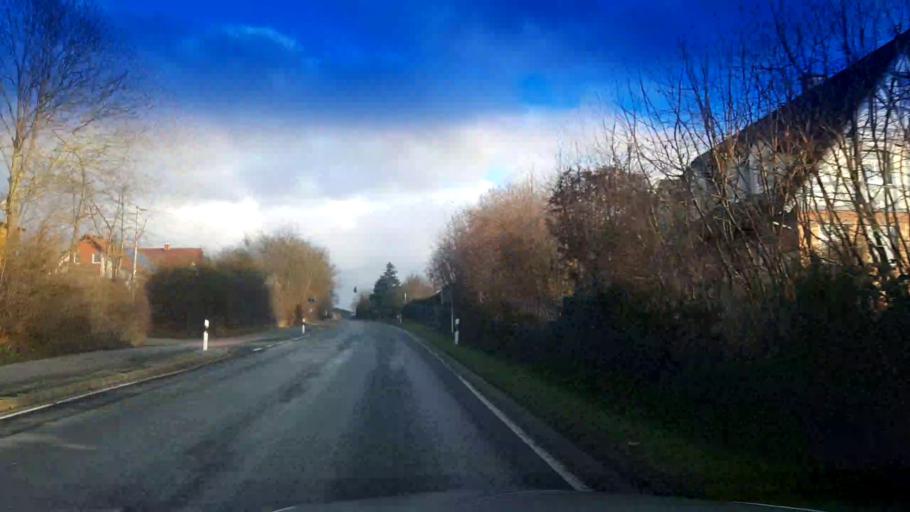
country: DE
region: Bavaria
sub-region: Upper Franconia
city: Buttenheim
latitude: 49.8263
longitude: 11.0211
